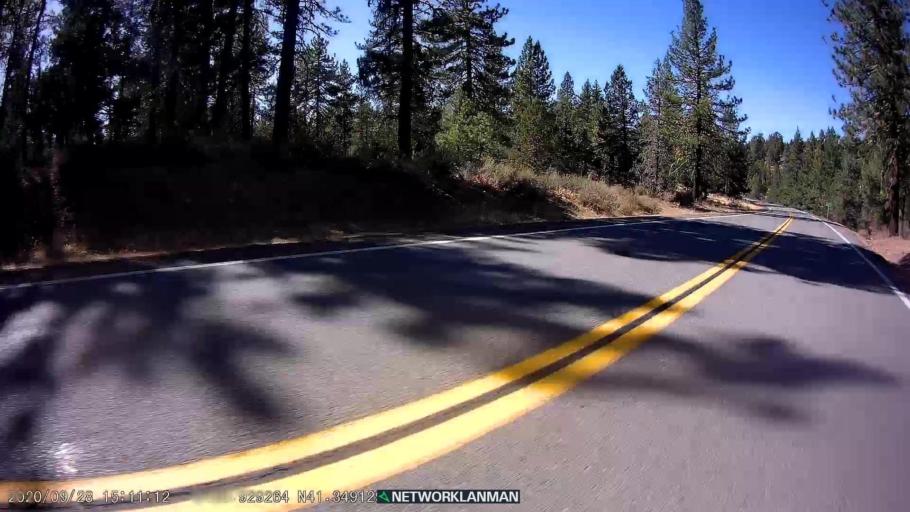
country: US
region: California
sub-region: Modoc County
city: Alturas
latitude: 41.3494
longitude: -120.9297
